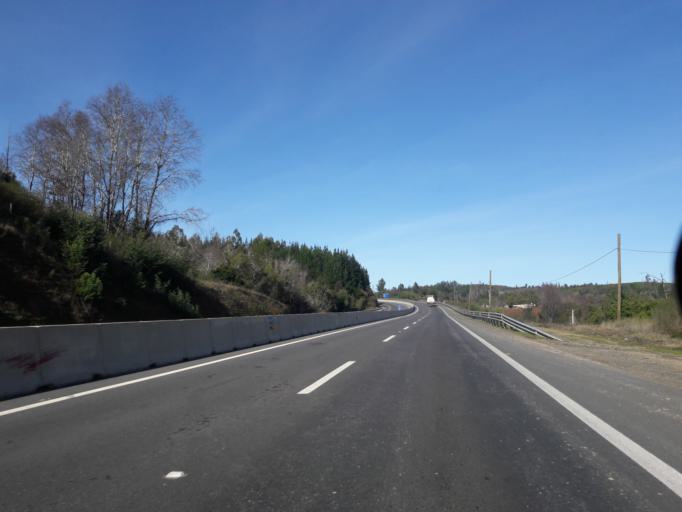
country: CL
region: Biobio
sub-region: Provincia de Concepcion
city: Chiguayante
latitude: -36.9213
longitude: -72.7734
